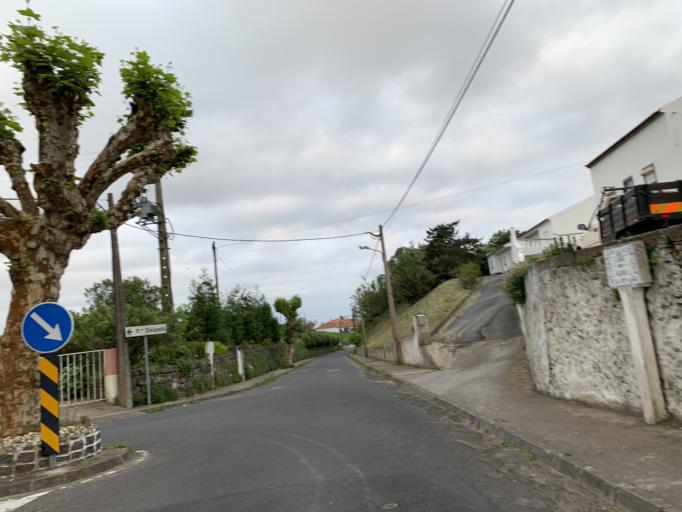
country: PT
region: Azores
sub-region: Ponta Delgada
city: Arrifes
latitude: 37.8472
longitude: -25.8401
